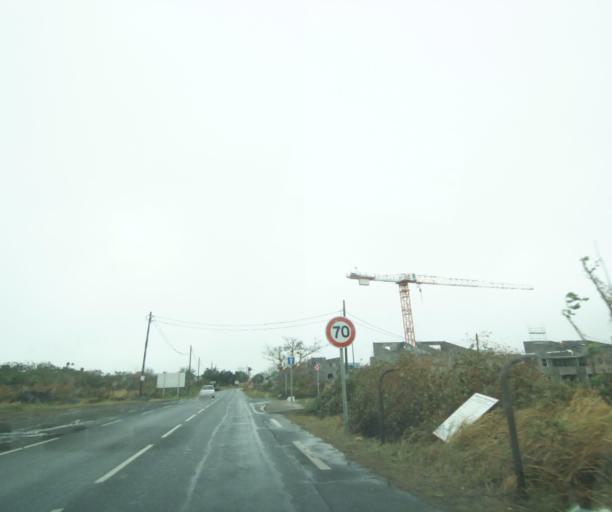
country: RE
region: Reunion
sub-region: Reunion
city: Saint-Paul
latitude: -21.0442
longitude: 55.2665
